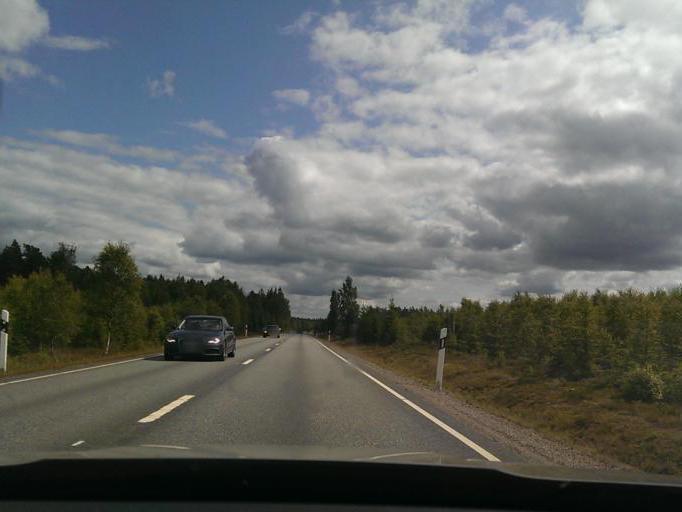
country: SE
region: Joenkoeping
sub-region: Varnamo Kommun
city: Varnamo
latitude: 57.2647
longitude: 13.9734
